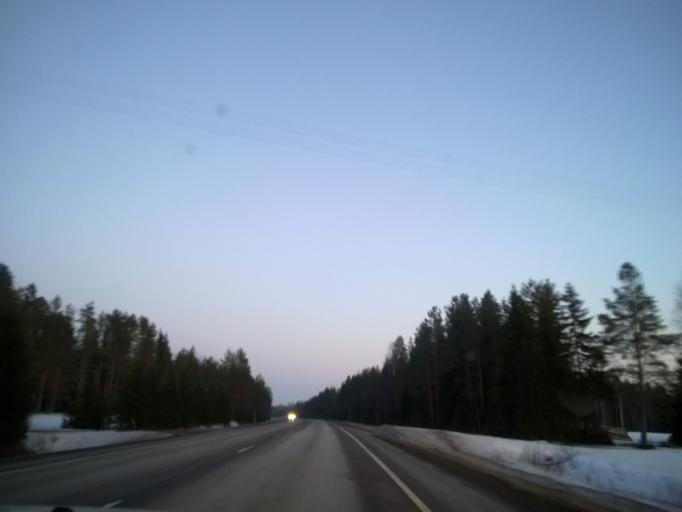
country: FI
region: Northern Ostrobothnia
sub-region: Nivala-Haapajaervi
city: Pyhaesalmi
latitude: 63.7895
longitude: 25.9220
